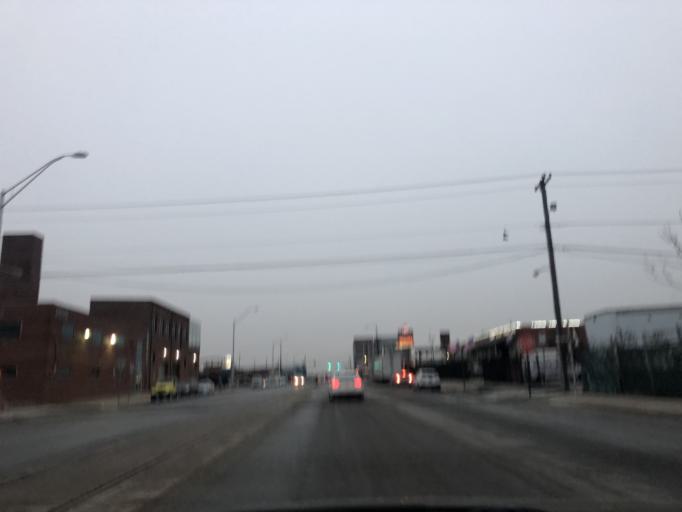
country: US
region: Pennsylvania
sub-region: Philadelphia County
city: Philadelphia
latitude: 39.9896
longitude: -75.1366
